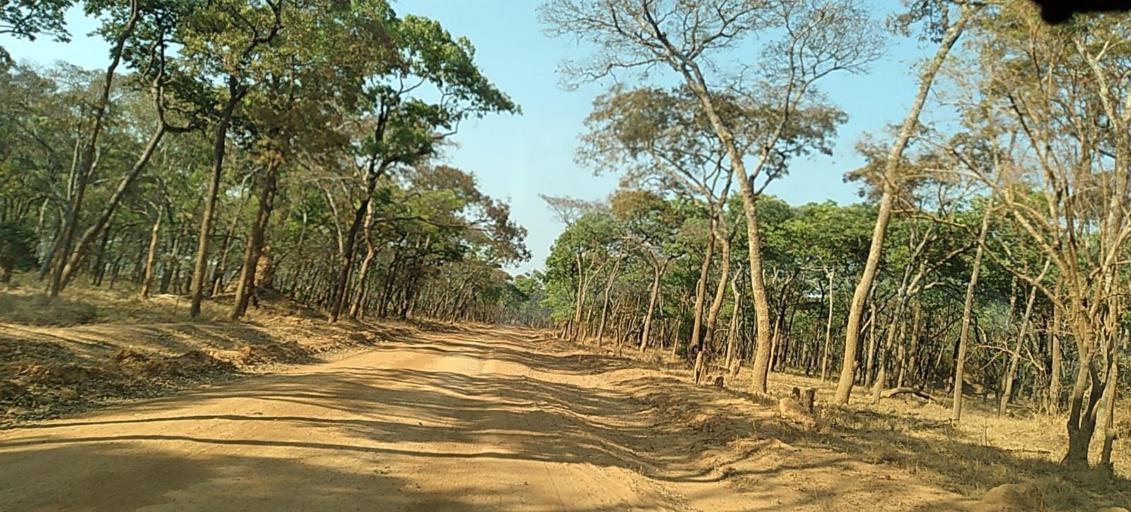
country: ZM
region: North-Western
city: Kasempa
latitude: -13.6001
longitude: 25.9794
